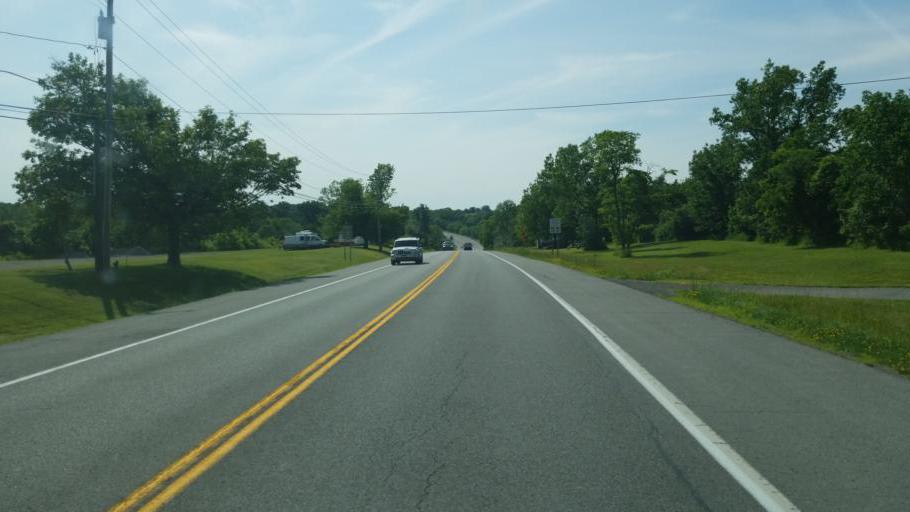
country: US
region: New York
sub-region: Monroe County
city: Honeoye Falls
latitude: 42.9074
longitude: -77.5511
